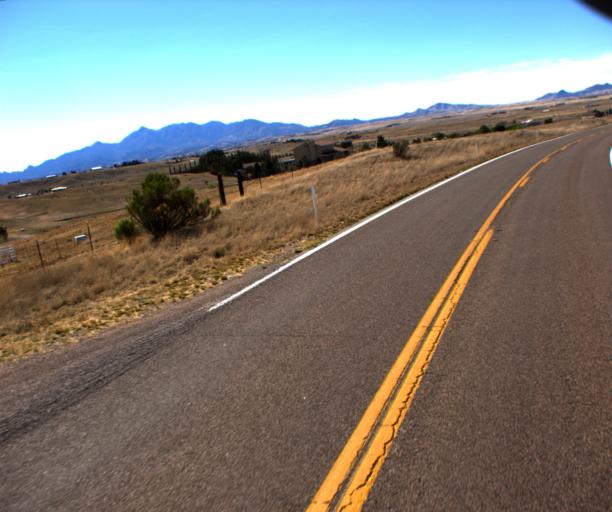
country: US
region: Arizona
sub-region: Cochise County
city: Huachuca City
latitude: 31.6687
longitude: -110.6072
